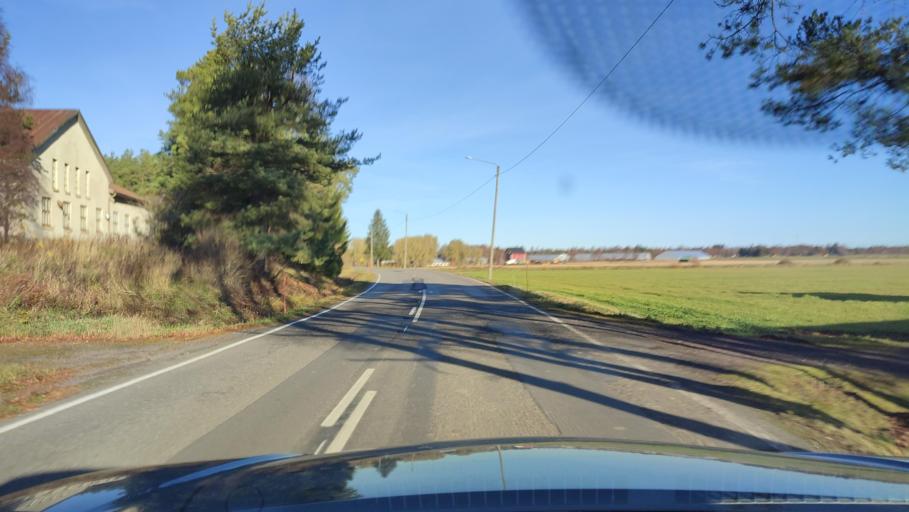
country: FI
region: Southern Ostrobothnia
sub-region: Suupohja
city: Teuva
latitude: 62.4633
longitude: 21.7140
